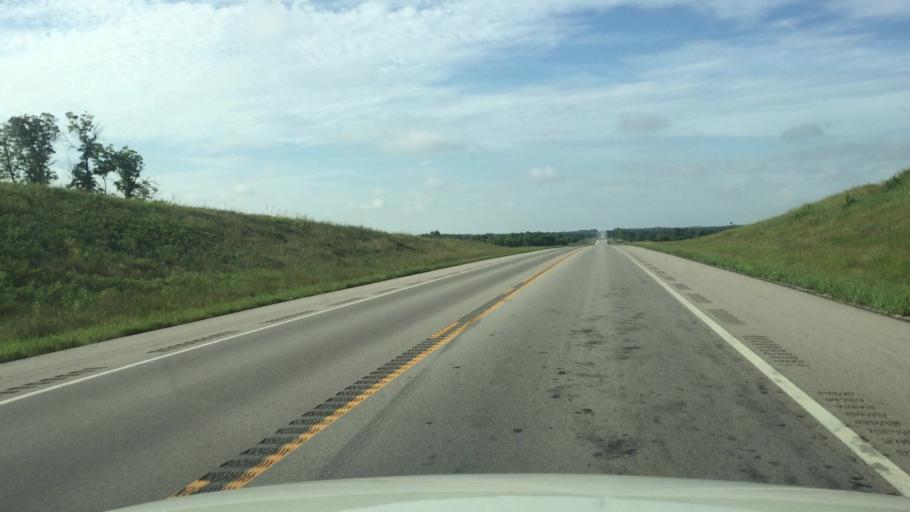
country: US
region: Kansas
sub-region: Allen County
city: Iola
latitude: 38.0114
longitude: -95.3807
